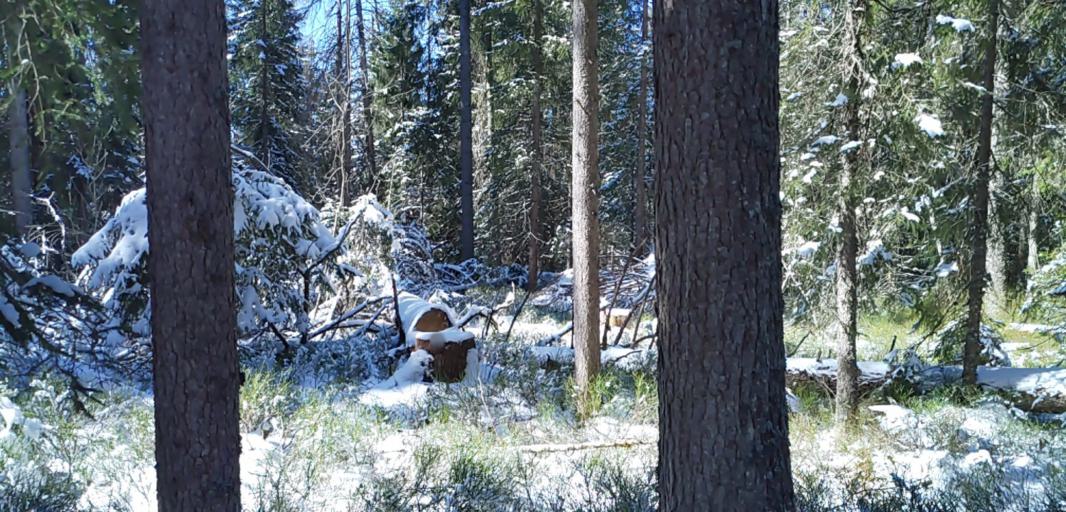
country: CH
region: Bern
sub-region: Jura bernois
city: Tramelan
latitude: 47.2402
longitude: 7.0517
